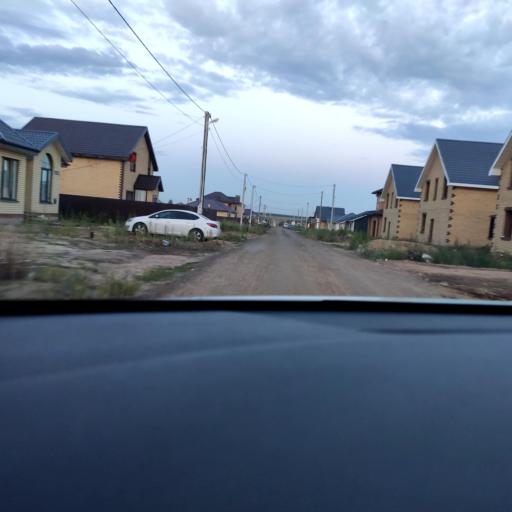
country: RU
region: Tatarstan
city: Stolbishchi
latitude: 55.7164
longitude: 49.3001
